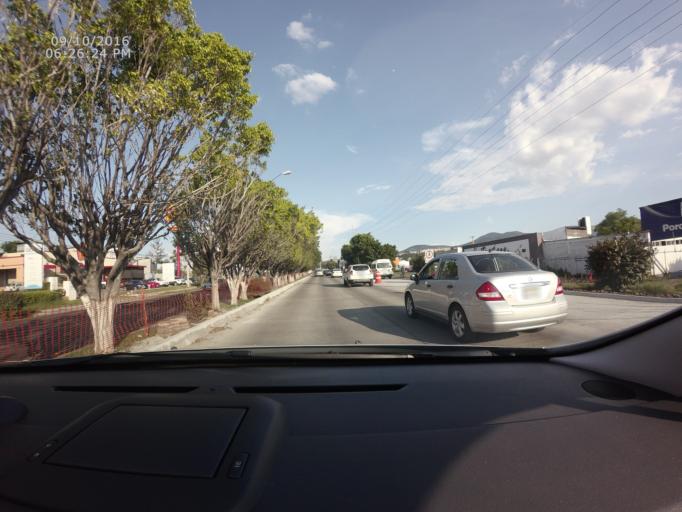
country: MX
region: Michoacan
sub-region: Morelia
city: Morelos
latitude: 19.6750
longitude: -101.2159
